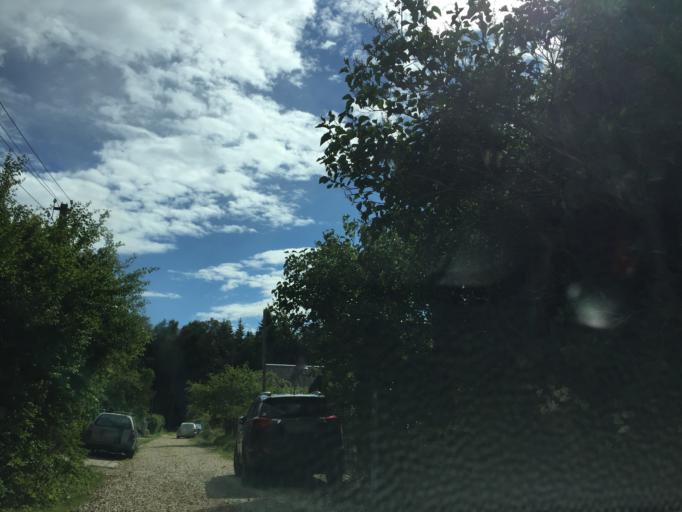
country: LV
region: Carnikava
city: Carnikava
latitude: 57.1180
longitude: 24.2245
